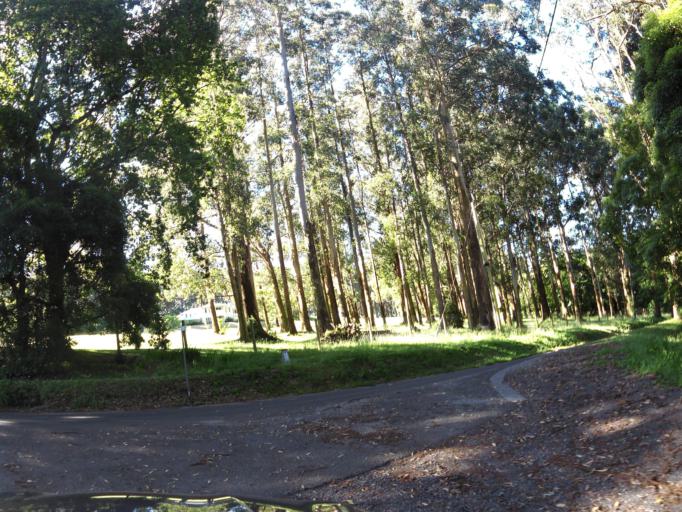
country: AU
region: Victoria
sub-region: Yarra Ranges
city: Ferny Creek
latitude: -37.8799
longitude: 145.3374
